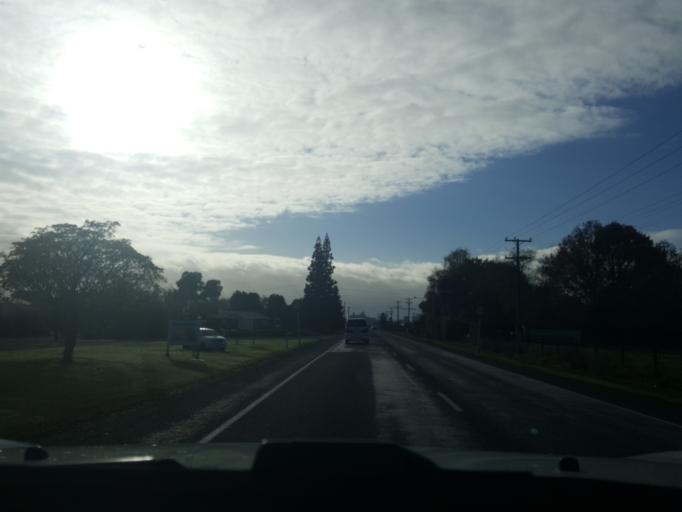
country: NZ
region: Waikato
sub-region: Waipa District
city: Cambridge
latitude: -37.6638
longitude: 175.5115
